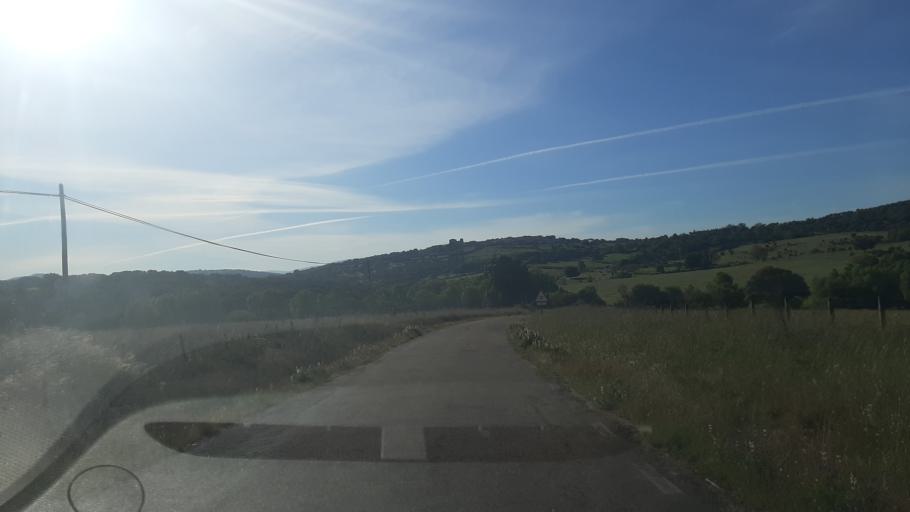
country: ES
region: Castille and Leon
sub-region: Provincia de Salamanca
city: Guijo de Avila
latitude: 40.5370
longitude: -5.6548
